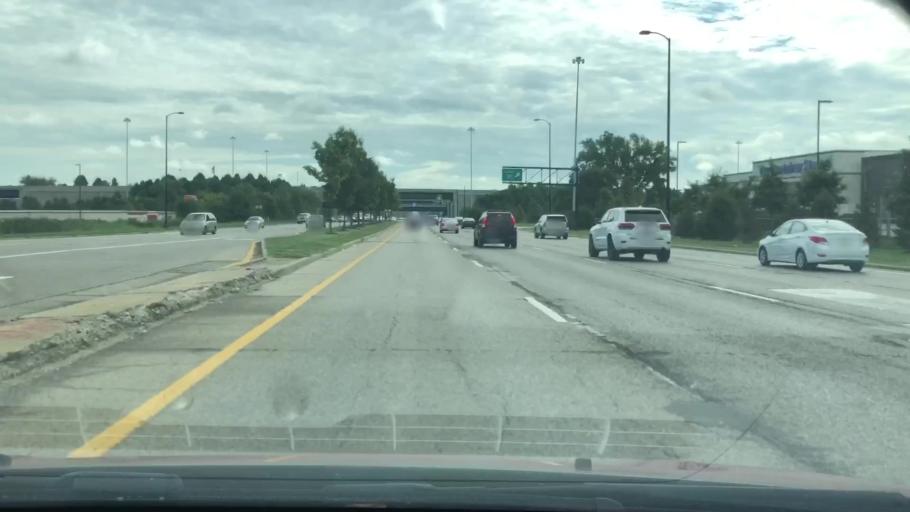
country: US
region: Ohio
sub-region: Franklin County
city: Huber Ridge
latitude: 40.0574
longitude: -82.9083
